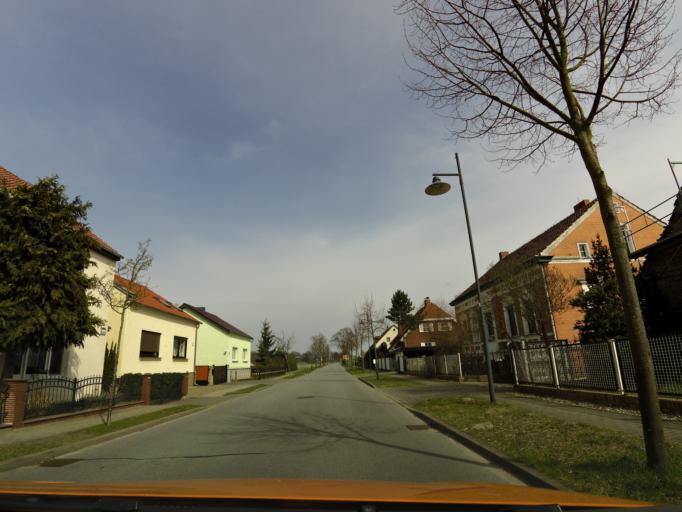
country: DE
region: Brandenburg
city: Stahnsdorf
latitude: 52.3292
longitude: 13.1685
